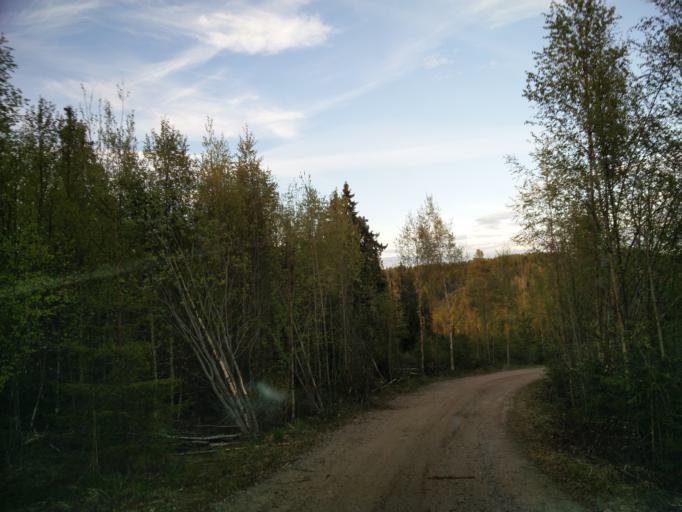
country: SE
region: Vaesternorrland
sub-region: Sundsvalls Kommun
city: Matfors
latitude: 62.3949
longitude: 16.8077
